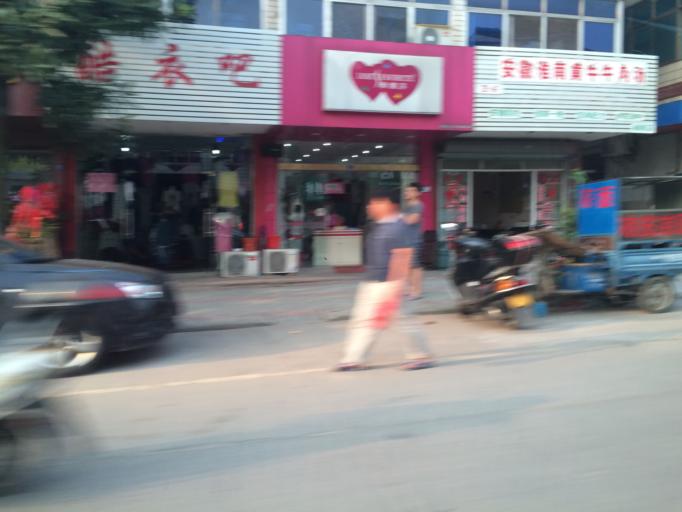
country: CN
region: Jiangsu Sheng
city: Xuxiake
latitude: 31.8124
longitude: 120.3018
